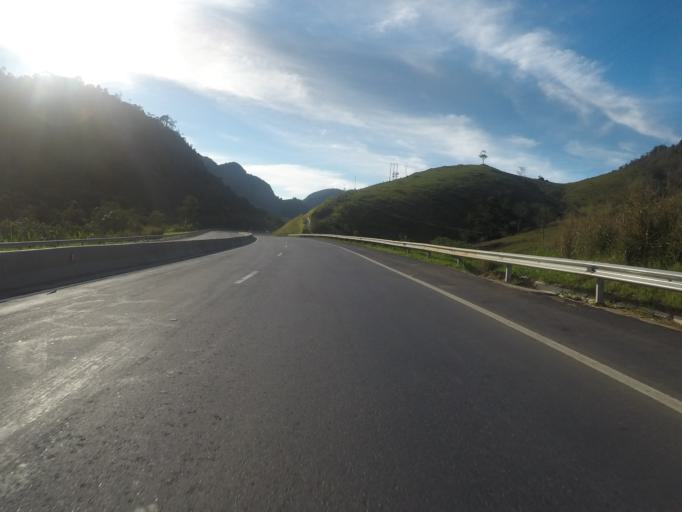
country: BR
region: Espirito Santo
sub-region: Ibiracu
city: Ibiracu
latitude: -19.8536
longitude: -40.3822
